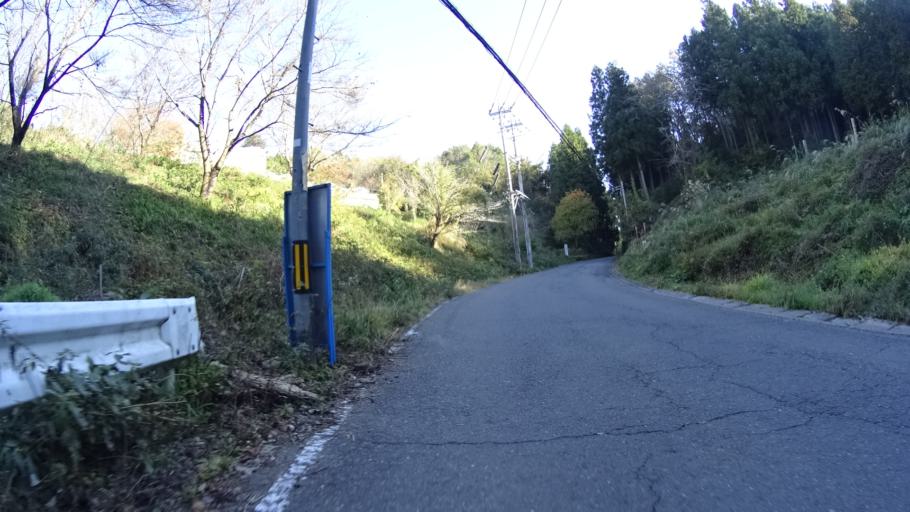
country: JP
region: Yamanashi
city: Uenohara
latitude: 35.6409
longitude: 139.1305
